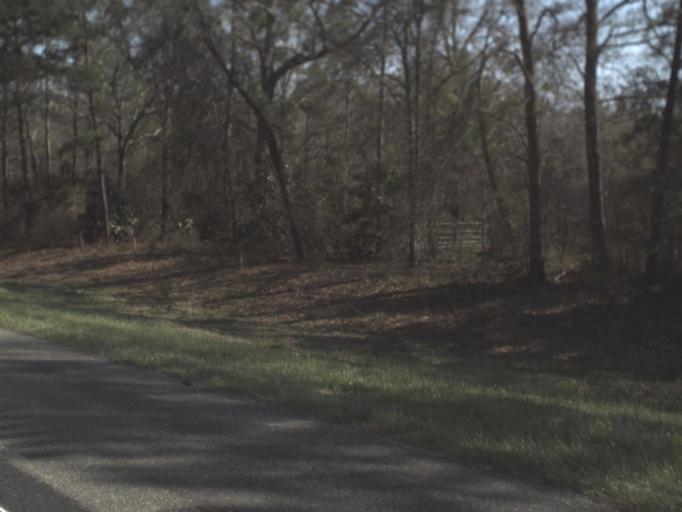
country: US
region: Florida
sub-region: Gadsden County
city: Gretna
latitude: 30.5753
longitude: -84.6903
